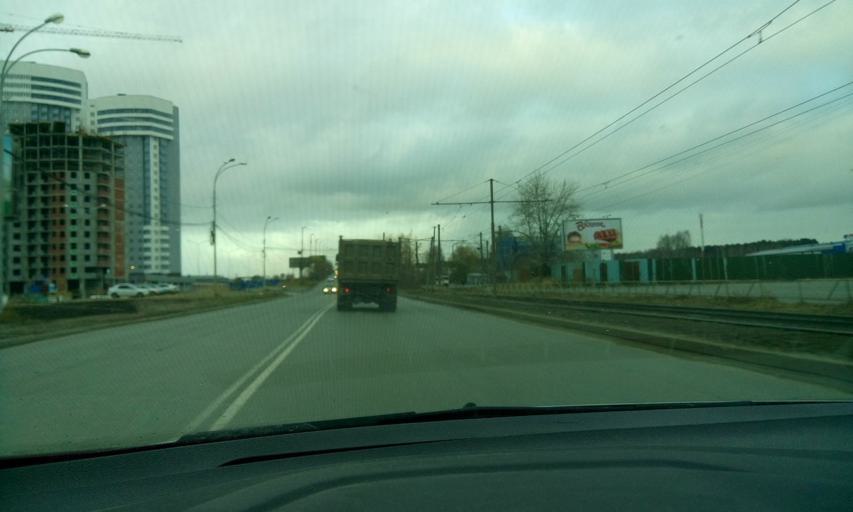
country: RU
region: Sverdlovsk
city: Yekaterinburg
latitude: 56.8631
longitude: 60.6658
